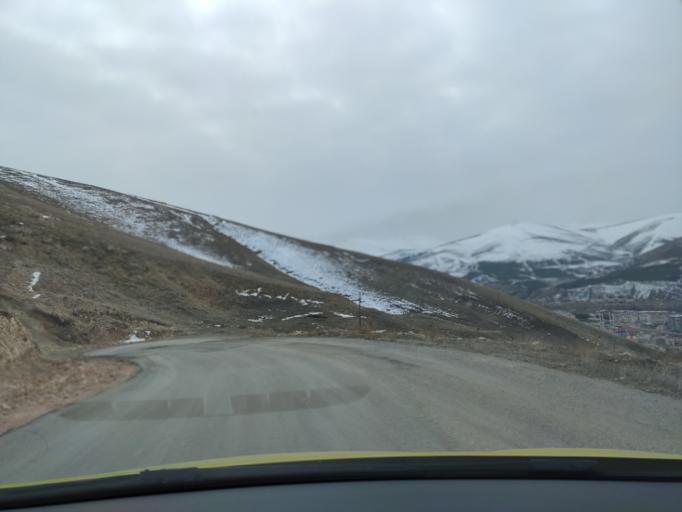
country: TR
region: Bayburt
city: Bayburt
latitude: 40.2581
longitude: 40.2411
